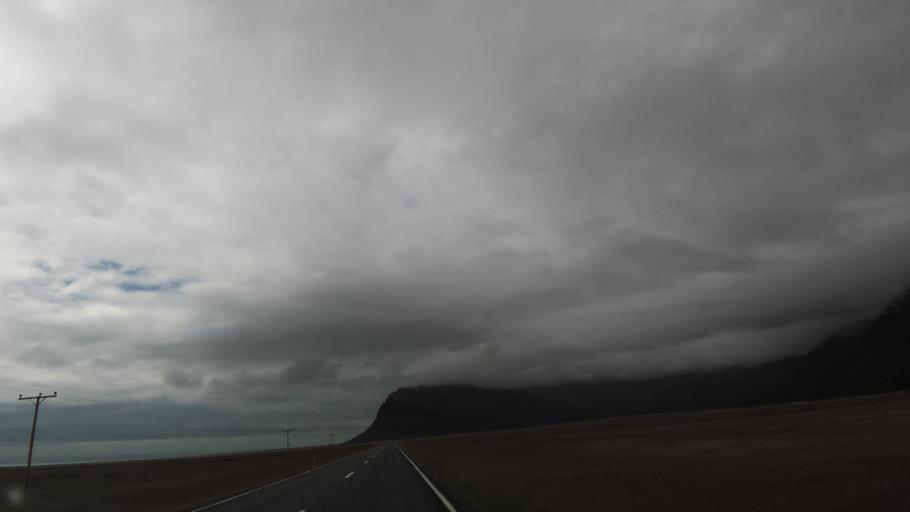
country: IS
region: East
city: Hoefn
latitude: 64.1682
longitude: -15.9101
